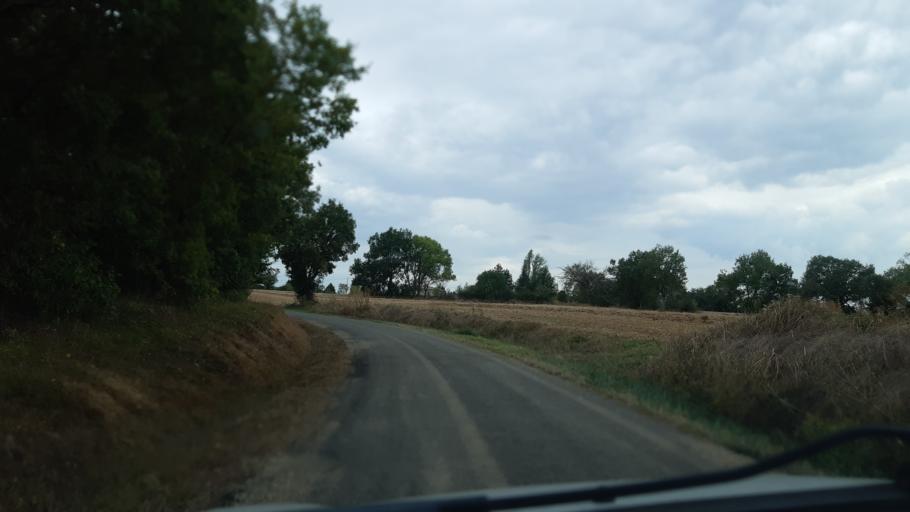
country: FR
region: Midi-Pyrenees
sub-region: Departement du Gers
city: Gimont
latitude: 43.6831
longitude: 0.9590
